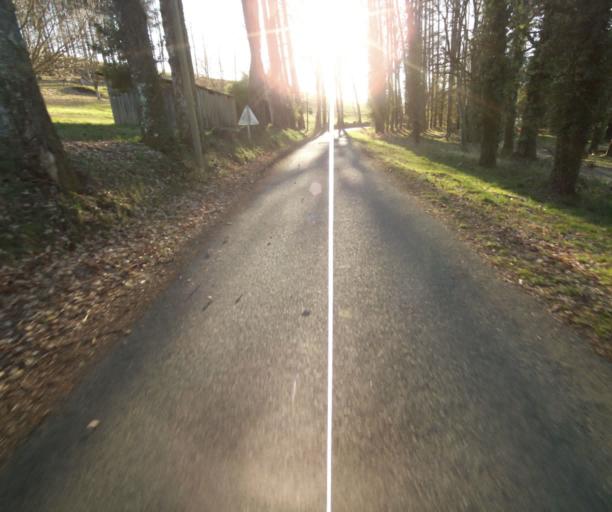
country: FR
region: Limousin
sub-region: Departement de la Correze
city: Seilhac
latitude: 45.3677
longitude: 1.6971
